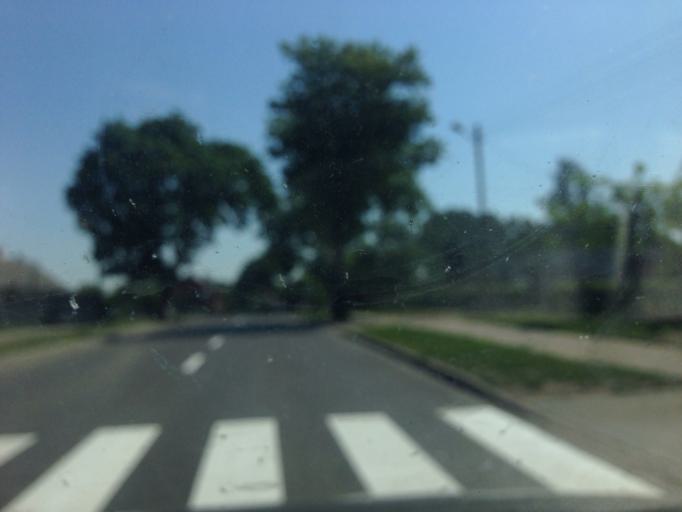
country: PL
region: Pomeranian Voivodeship
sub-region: Powiat tczewski
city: Pelplin
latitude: 53.9271
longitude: 18.6830
